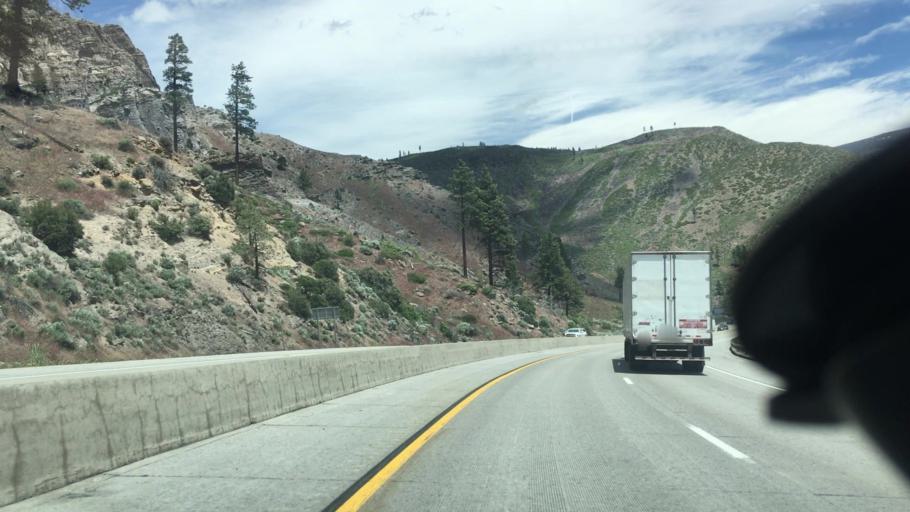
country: US
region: Nevada
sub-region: Washoe County
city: Incline Village
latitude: 39.3763
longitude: -120.0304
